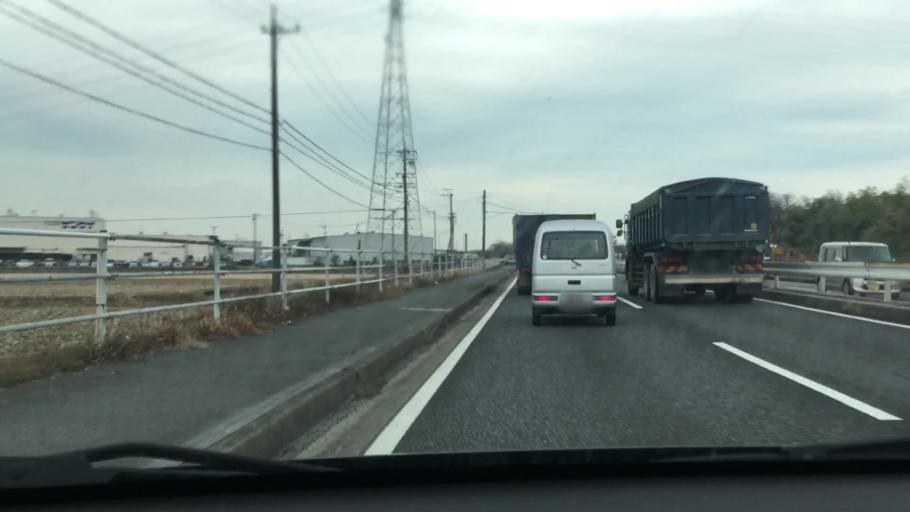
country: JP
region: Mie
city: Suzuka
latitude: 34.8903
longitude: 136.5370
